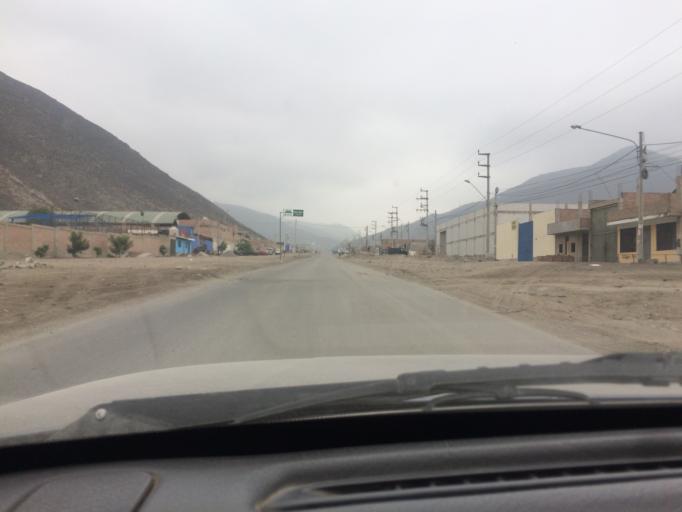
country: PE
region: Lima
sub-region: Lima
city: Cieneguilla
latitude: -12.1673
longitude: -76.8649
